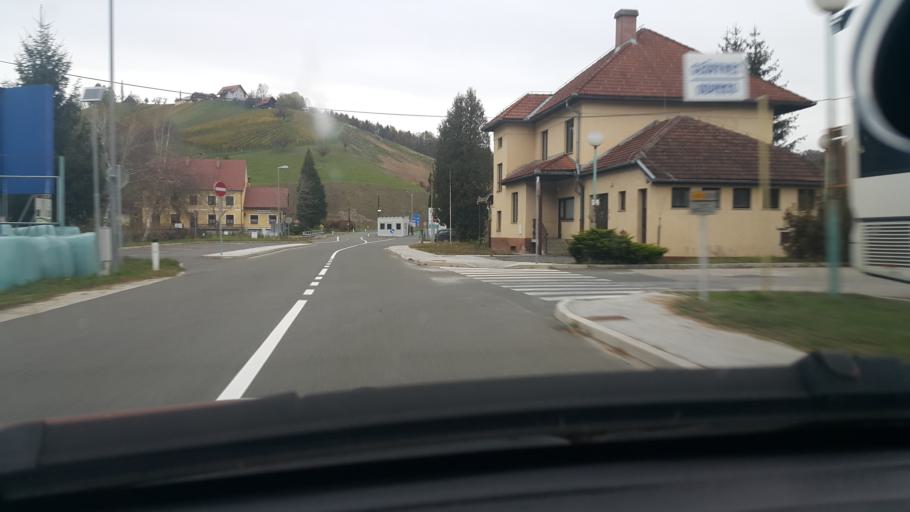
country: AT
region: Styria
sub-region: Politischer Bezirk Leibnitz
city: Sulztal an der Weinstrasse
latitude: 46.6469
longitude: 15.5520
